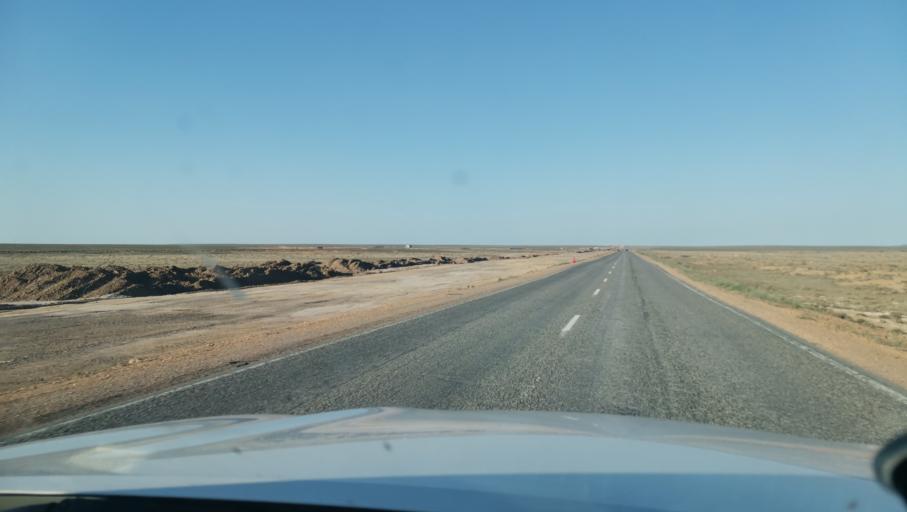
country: KZ
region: Qaraghandy
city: Saryshaghan
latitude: 46.4076
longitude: 73.8924
